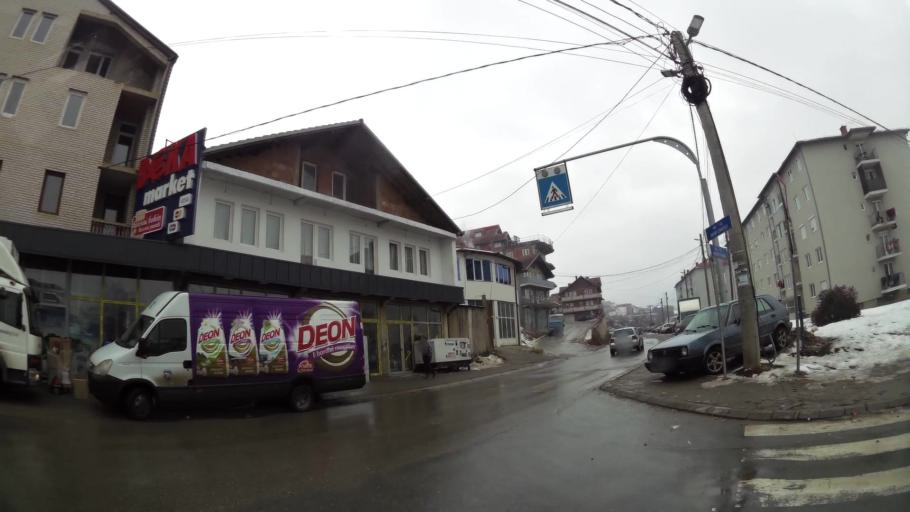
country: XK
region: Pristina
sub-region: Komuna e Prishtines
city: Pristina
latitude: 42.6821
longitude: 21.1740
